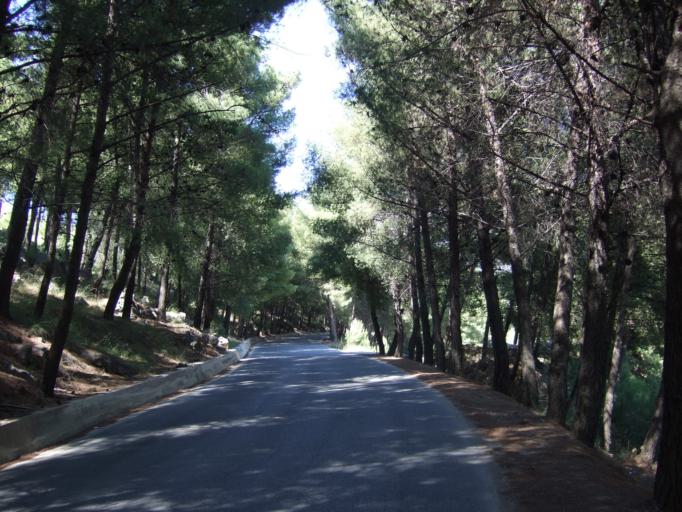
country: AL
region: Durres
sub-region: Rrethi i Krujes
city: Kruje
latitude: 41.4944
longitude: 19.7734
